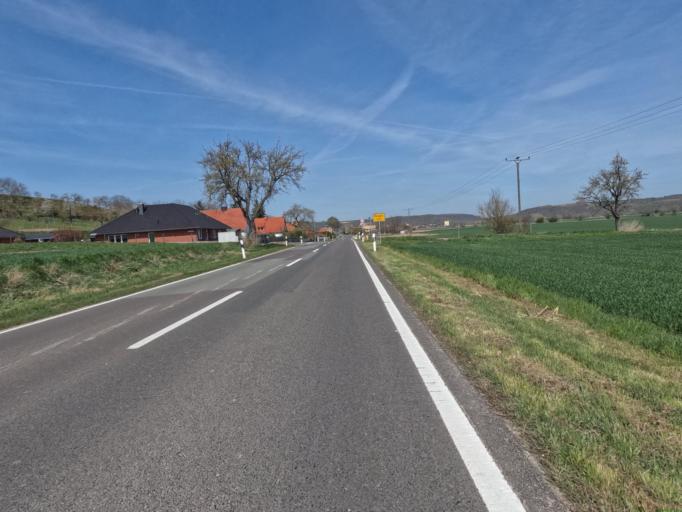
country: DE
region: Saxony-Anhalt
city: Beesenstedt
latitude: 51.5980
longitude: 11.7521
